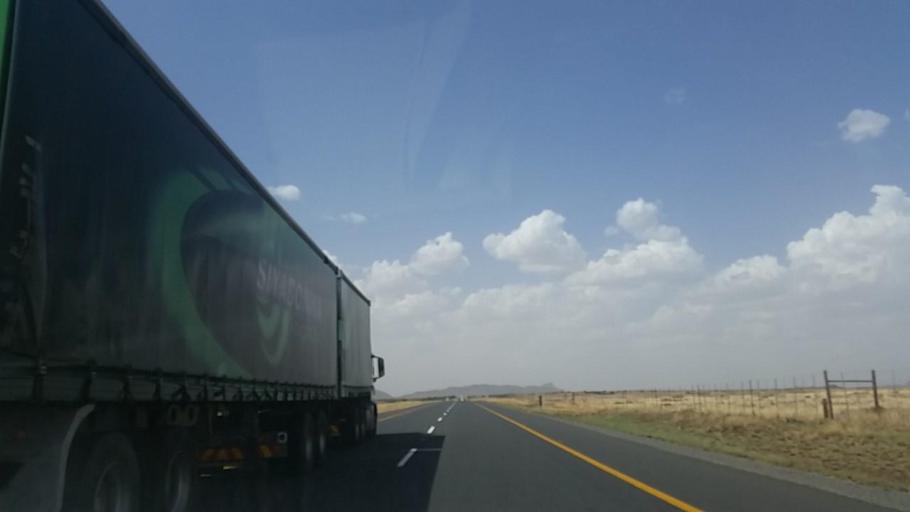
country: ZA
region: Northern Cape
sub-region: Pixley ka Seme District Municipality
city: Colesberg
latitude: -30.5800
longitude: 25.4318
